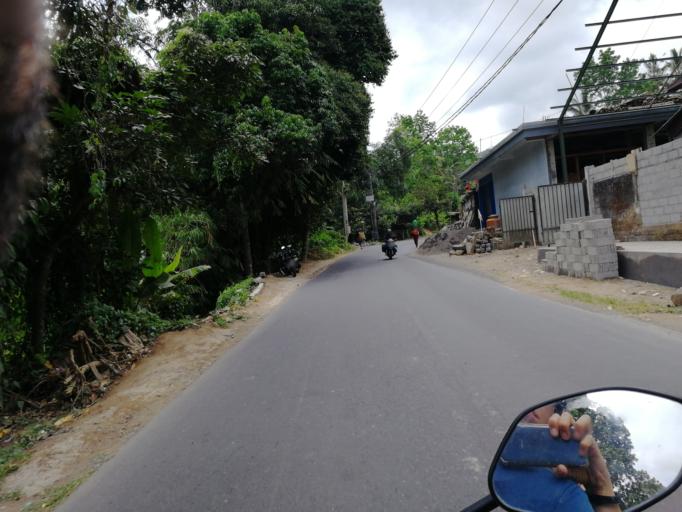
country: ID
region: Bali
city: Banjar Wates Tengah
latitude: -8.4528
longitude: 115.4550
